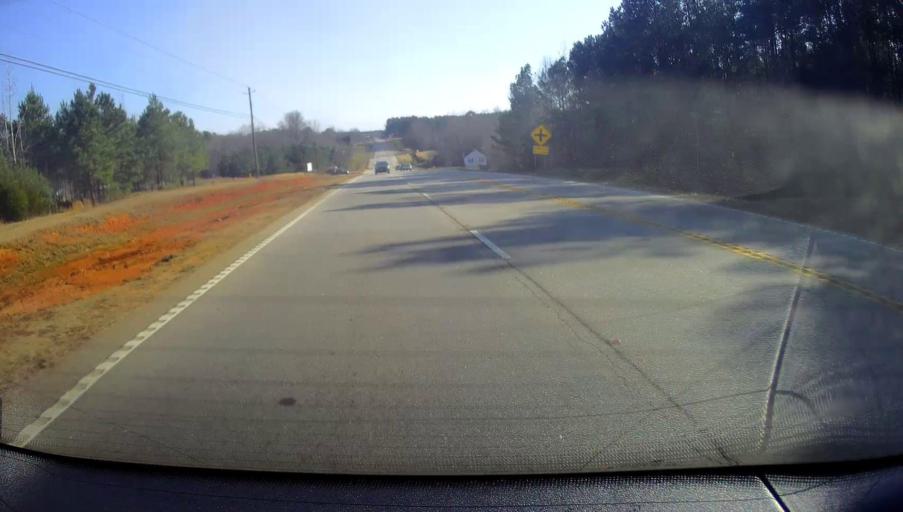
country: US
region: Georgia
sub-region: Butts County
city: Jackson
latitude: 33.3146
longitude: -83.9841
